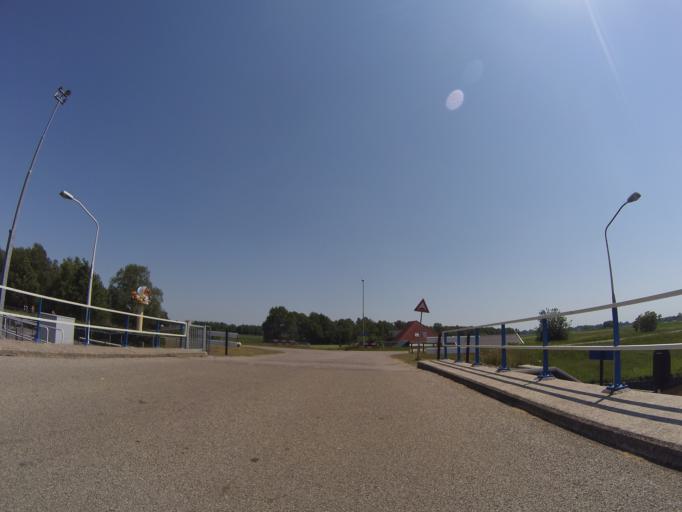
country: NL
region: Drenthe
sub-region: Gemeente Emmen
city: Schoonebeek
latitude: 52.6895
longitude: 6.8540
